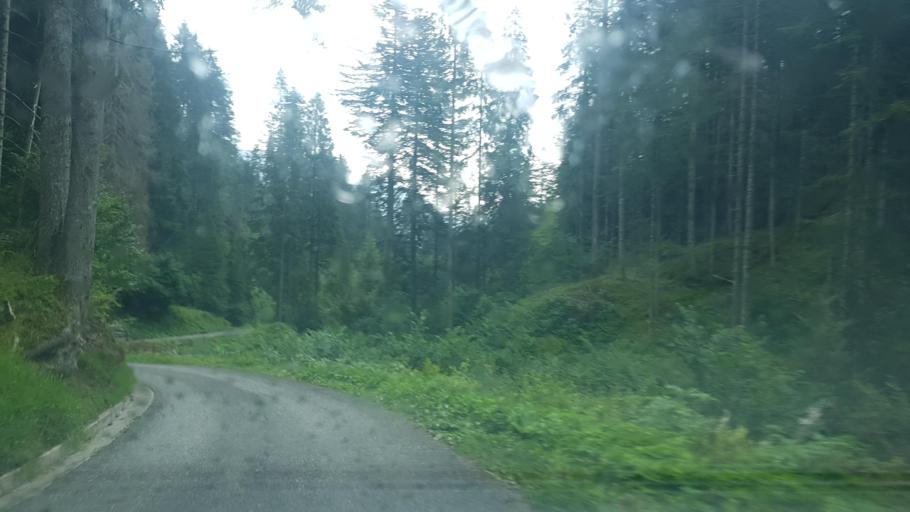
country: IT
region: Friuli Venezia Giulia
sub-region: Provincia di Udine
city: Rigolato
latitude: 46.5522
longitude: 12.8300
